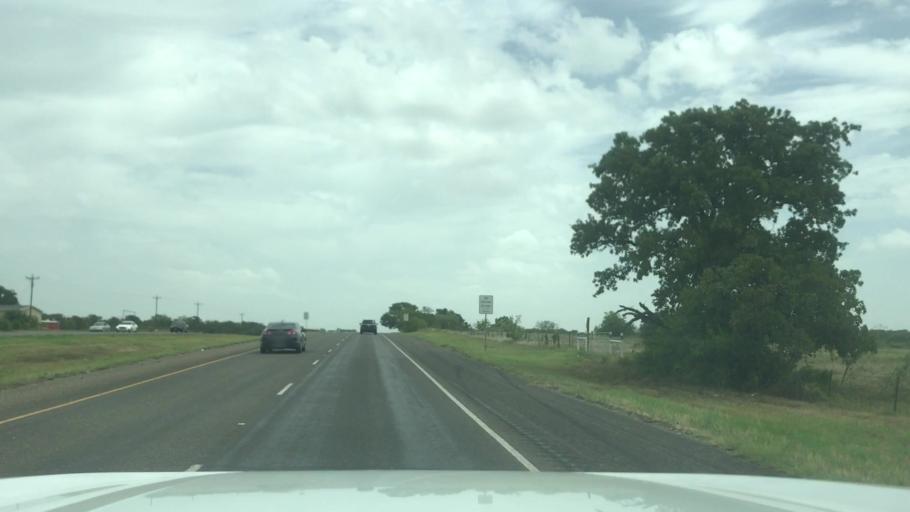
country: US
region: Texas
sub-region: McLennan County
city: Riesel
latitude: 31.4985
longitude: -96.9367
